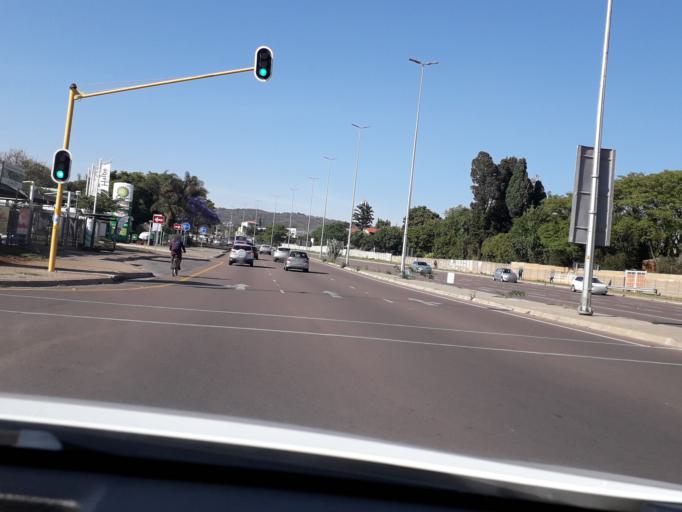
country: ZA
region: Gauteng
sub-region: City of Tshwane Metropolitan Municipality
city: Pretoria
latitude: -25.7542
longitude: 28.3246
